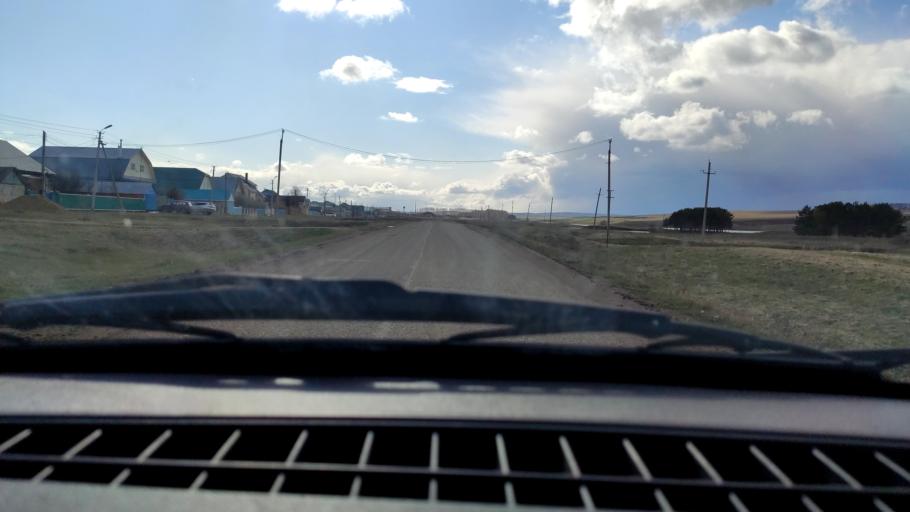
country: RU
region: Bashkortostan
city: Chekmagush
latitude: 55.1305
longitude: 54.6349
